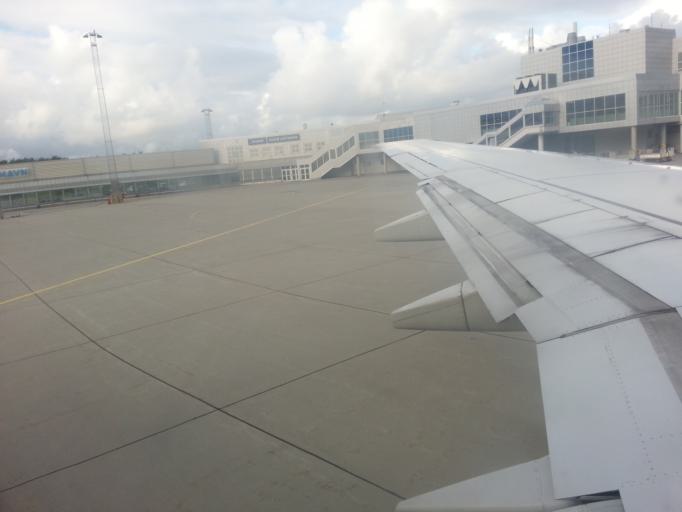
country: NO
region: Nordland
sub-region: Bodo
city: Bodo
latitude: 67.2718
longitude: 14.3665
